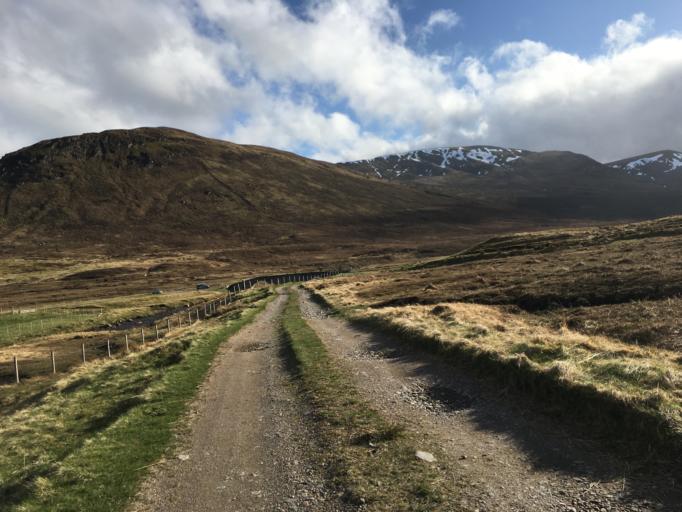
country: GB
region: Scotland
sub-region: Highland
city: Kingussie
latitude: 57.0221
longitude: -4.4353
